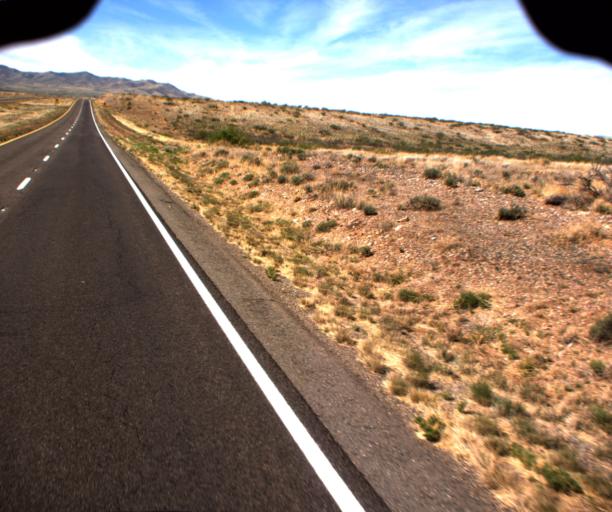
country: US
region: Arizona
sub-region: Cochise County
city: Willcox
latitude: 32.3718
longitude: -109.6742
